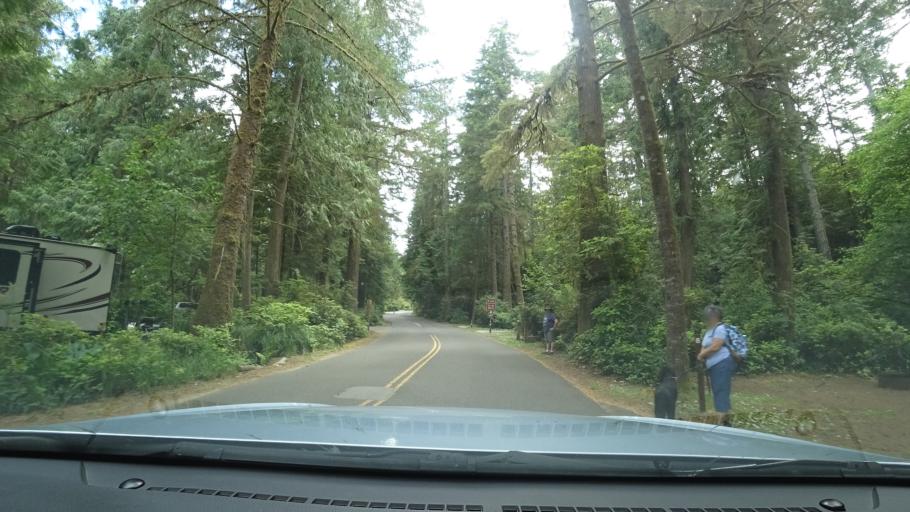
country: US
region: Oregon
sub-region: Lane County
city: Dunes City
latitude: 43.9245
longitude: -124.1119
